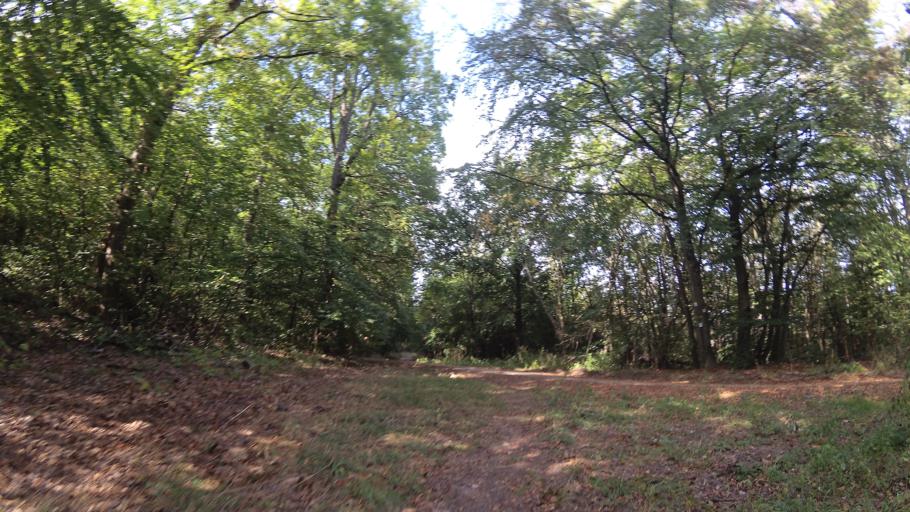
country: DE
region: Saarland
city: Sankt Wendel
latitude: 49.4740
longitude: 7.2041
